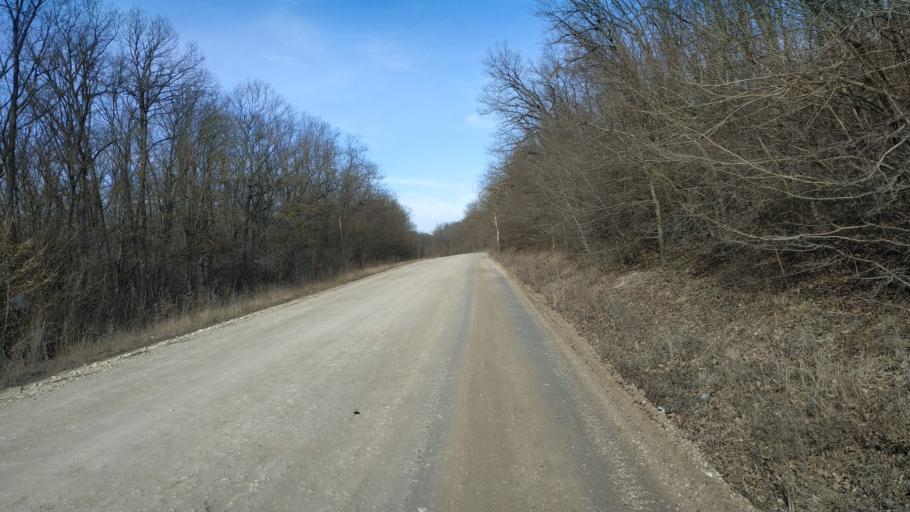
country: MD
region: Straseni
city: Straseni
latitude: 47.0370
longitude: 28.6133
